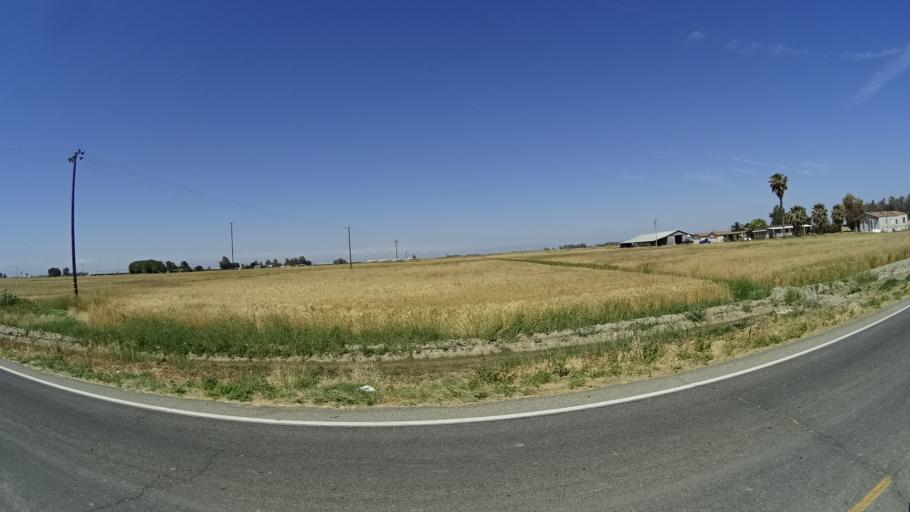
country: US
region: California
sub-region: Kings County
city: Stratford
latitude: 36.2359
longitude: -119.7806
